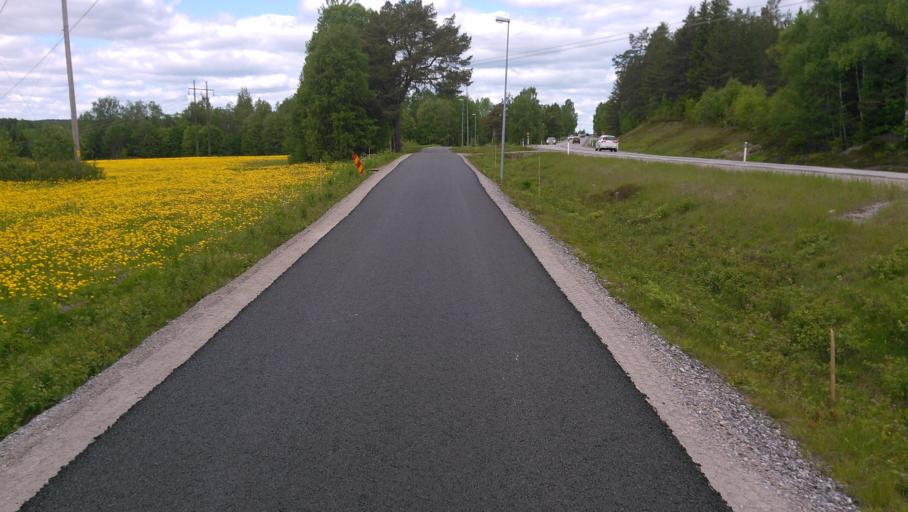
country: SE
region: Vaesterbotten
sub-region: Umea Kommun
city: Roback
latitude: 63.8556
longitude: 20.0966
